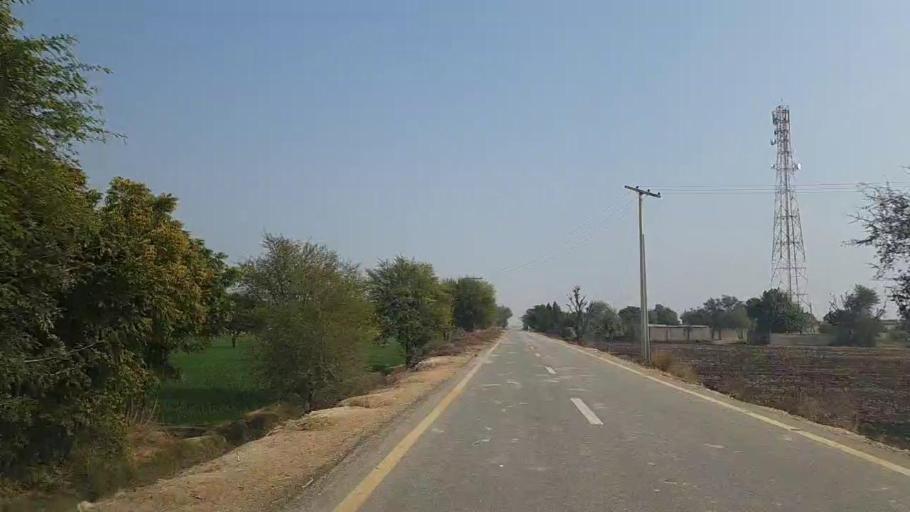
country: PK
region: Sindh
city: Jam Sahib
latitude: 26.3725
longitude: 68.5167
